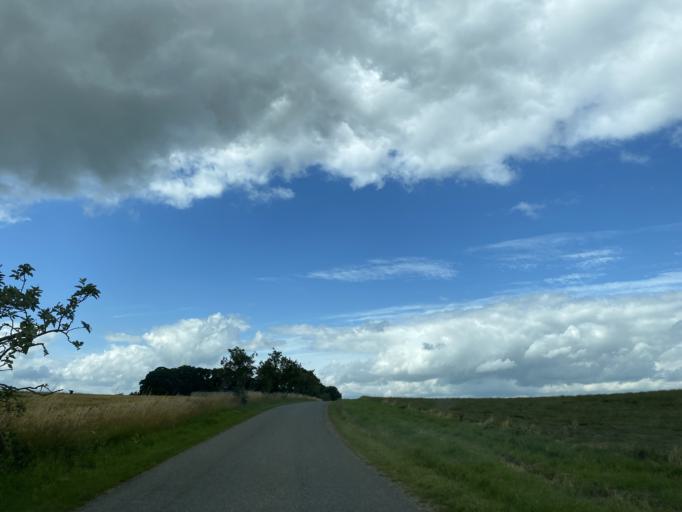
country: DK
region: Central Jutland
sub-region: Silkeborg Kommune
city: Svejbaek
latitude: 56.2391
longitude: 9.6312
